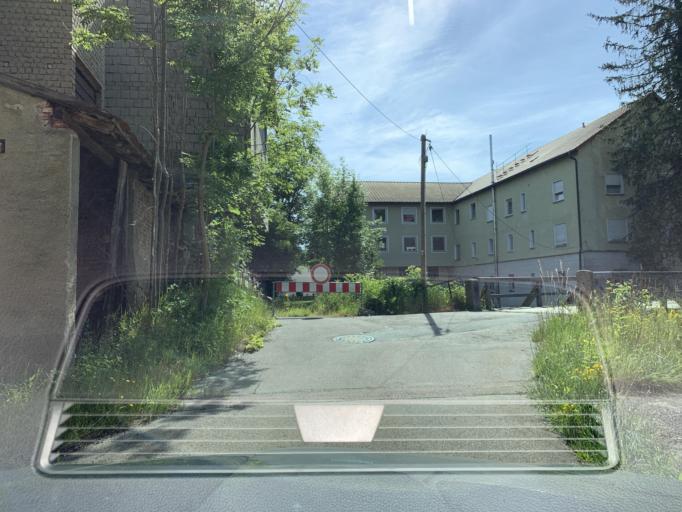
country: DE
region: Bavaria
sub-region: Upper Palatinate
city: Altendorf
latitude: 49.4038
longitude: 12.2821
